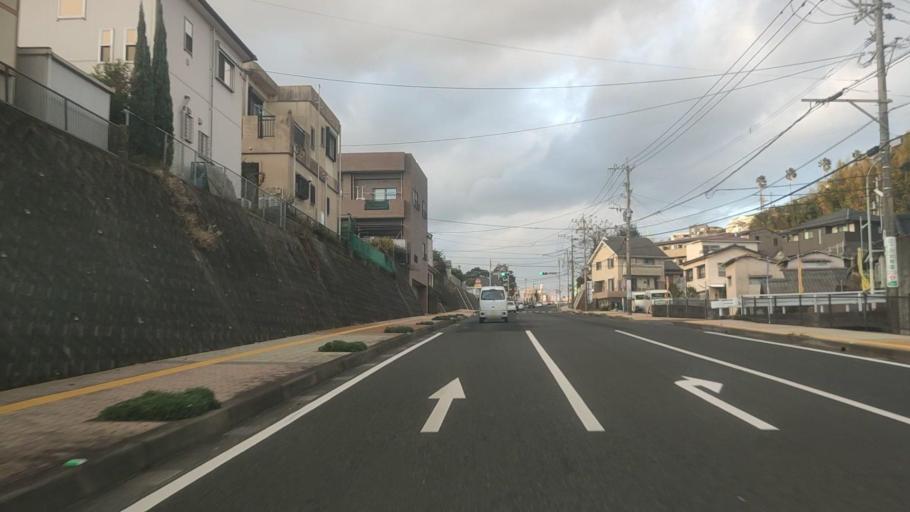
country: JP
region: Kagoshima
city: Kagoshima-shi
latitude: 31.6175
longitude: 130.5544
